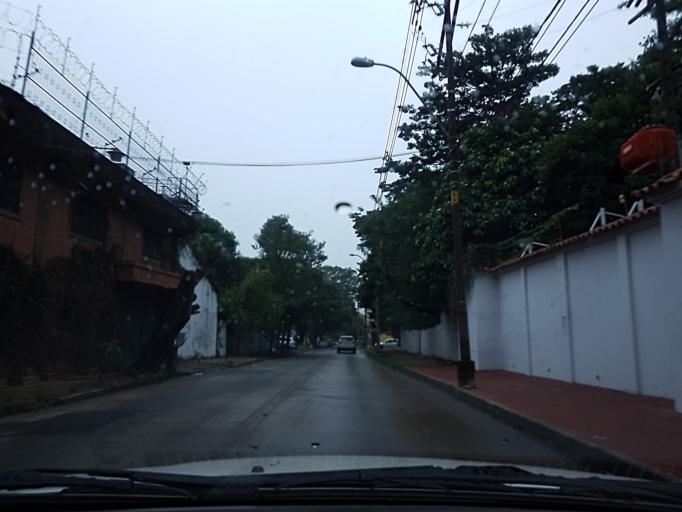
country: PY
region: Central
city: Lambare
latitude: -25.2995
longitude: -57.5809
